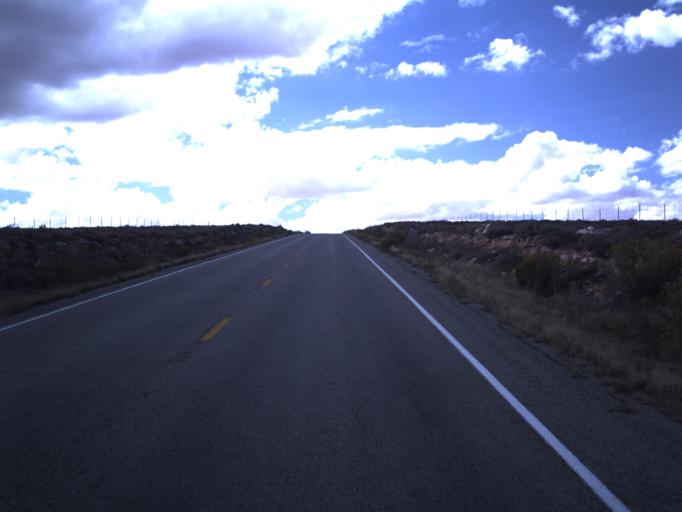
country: US
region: Utah
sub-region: San Juan County
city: Blanding
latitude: 37.2810
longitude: -109.7024
